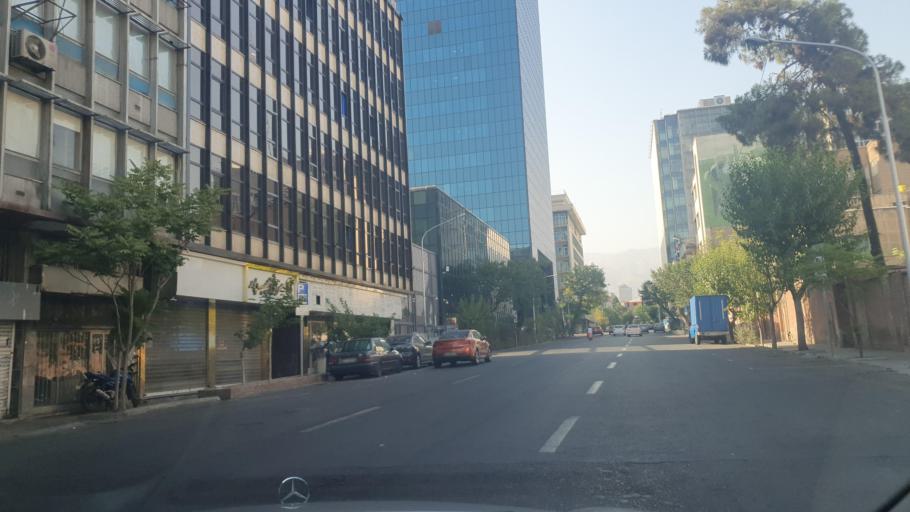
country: IR
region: Tehran
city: Tehran
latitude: 35.7056
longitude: 51.4212
